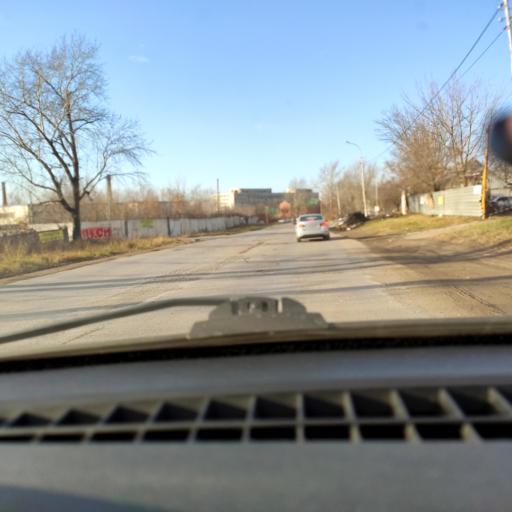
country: RU
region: Bashkortostan
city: Ufa
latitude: 54.8377
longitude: 56.0817
